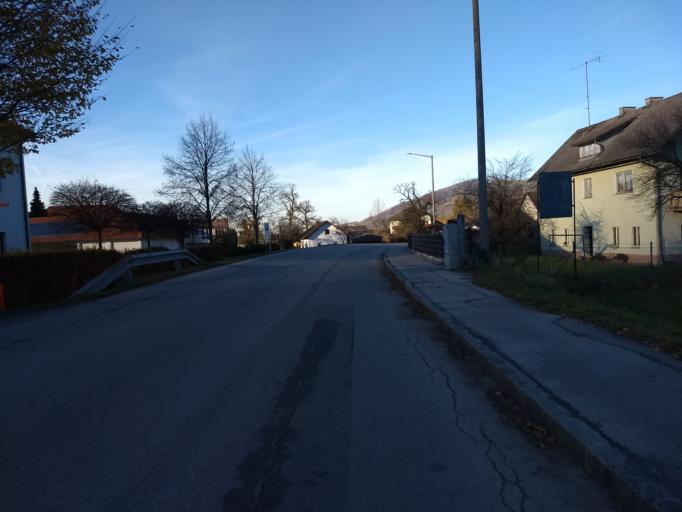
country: AT
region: Upper Austria
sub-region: Politischer Bezirk Kirchdorf an der Krems
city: Micheldorf in Oberoesterreich
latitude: 47.8812
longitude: 14.1326
